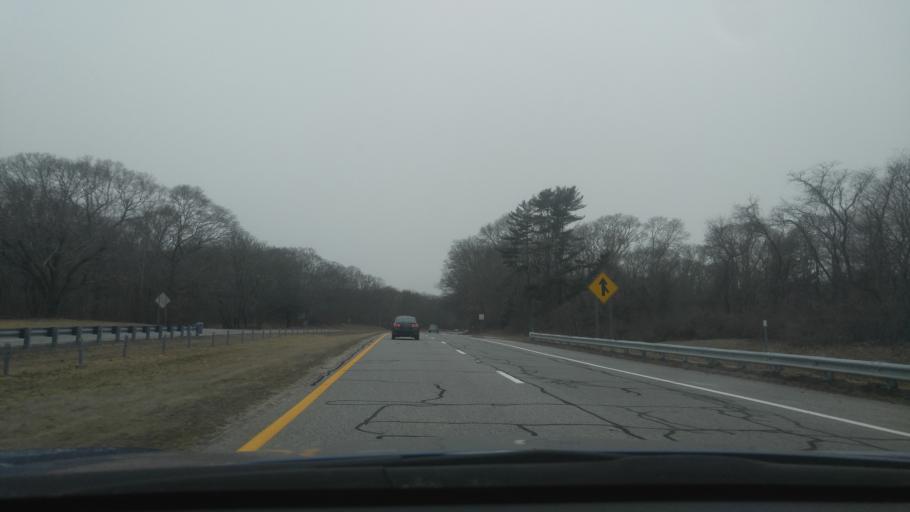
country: US
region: Rhode Island
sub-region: Washington County
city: Wakefield-Peacedale
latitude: 41.4279
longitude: -71.5011
